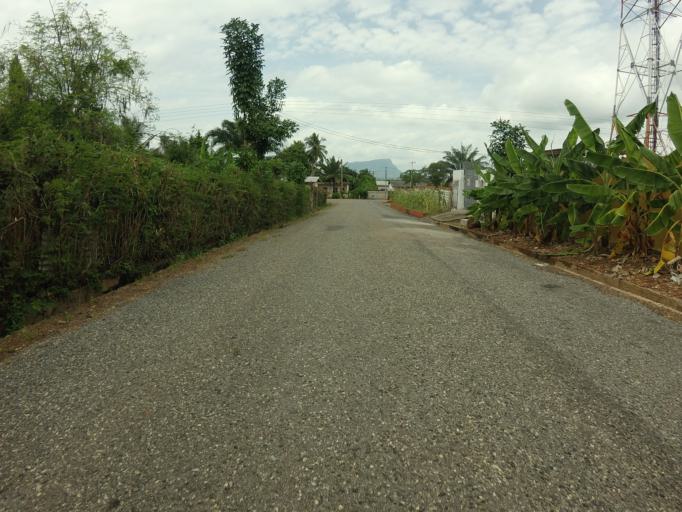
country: GH
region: Volta
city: Ho
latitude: 6.5935
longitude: 0.4757
